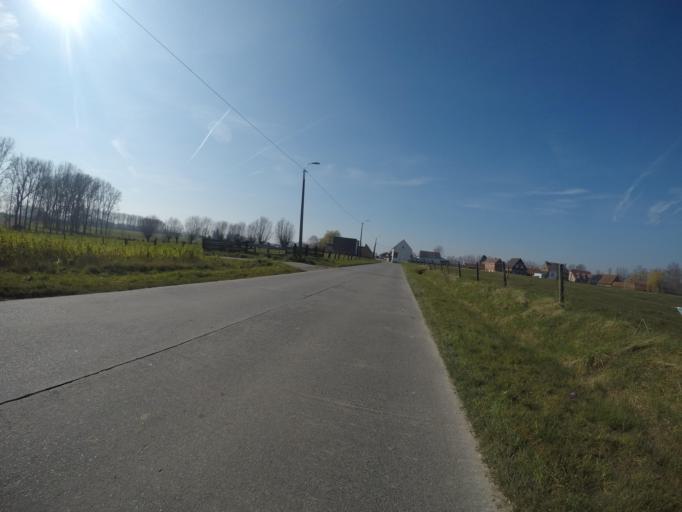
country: BE
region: Flanders
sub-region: Provincie Oost-Vlaanderen
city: Geraardsbergen
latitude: 50.7896
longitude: 3.8633
